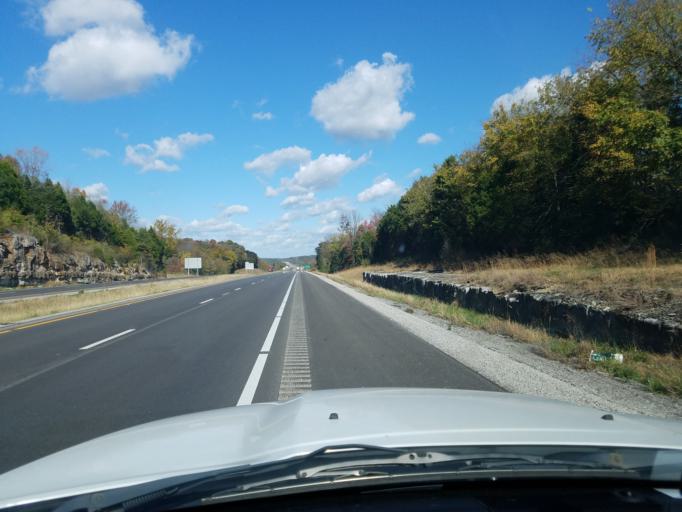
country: US
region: Kentucky
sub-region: Warren County
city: Bowling Green
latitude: 36.9684
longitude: -86.4990
